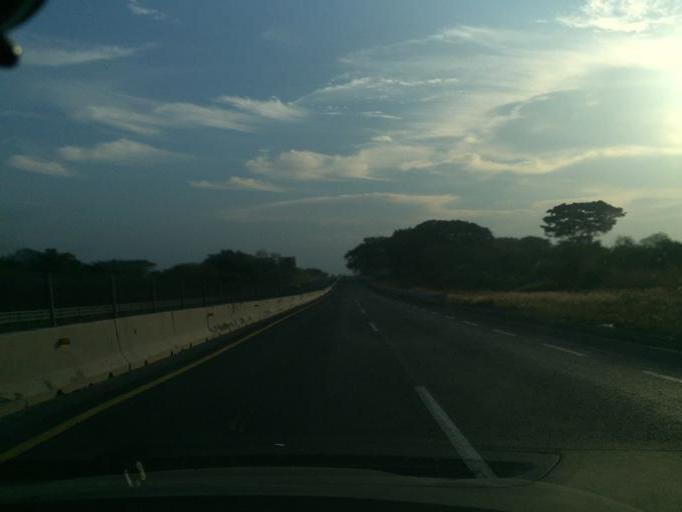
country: MX
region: Veracruz
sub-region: Tierra Blanca
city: Huixcolotla
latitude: 18.7849
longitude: -96.5326
